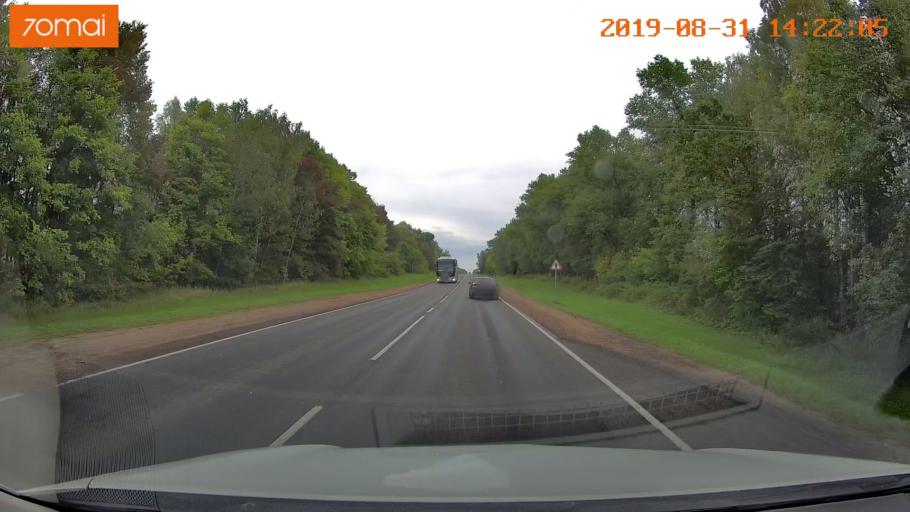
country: RU
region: Smolensk
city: Yekimovichi
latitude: 54.0893
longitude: 33.2101
